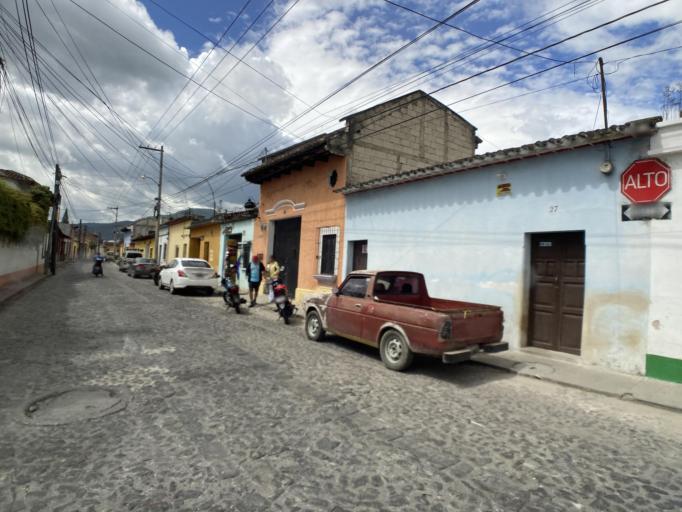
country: GT
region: Sacatepequez
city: Antigua Guatemala
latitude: 14.5527
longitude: -90.7405
